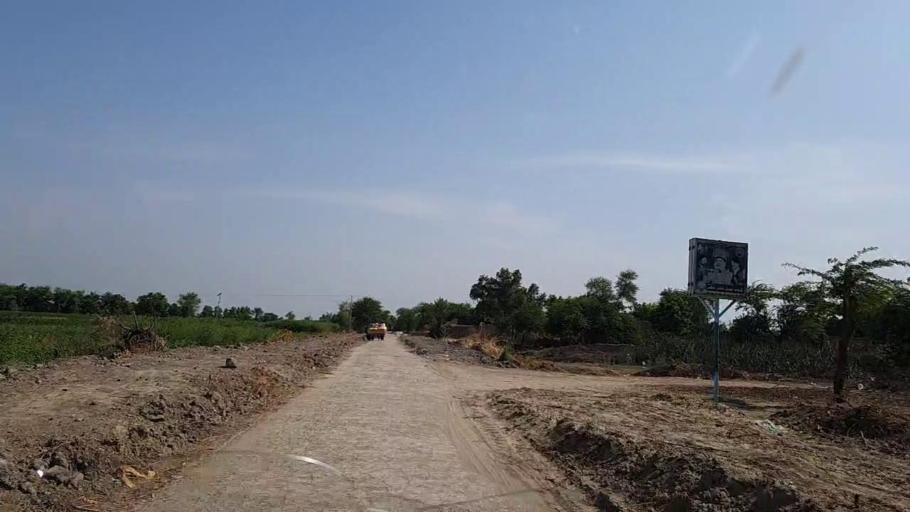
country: PK
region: Sindh
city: Khanpur
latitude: 27.7461
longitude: 69.3413
